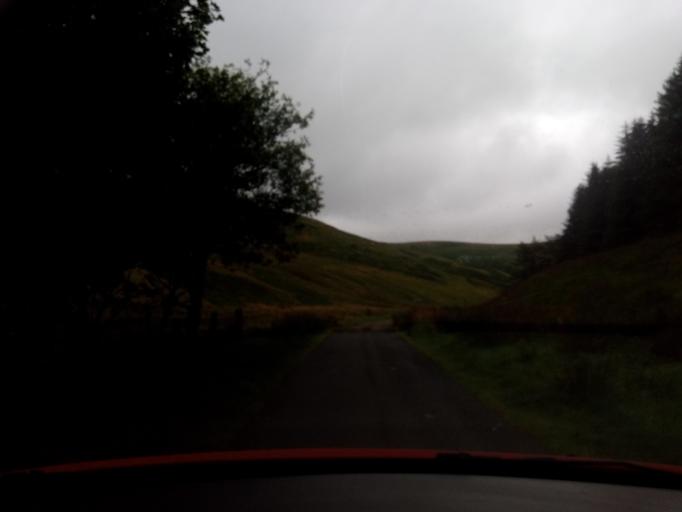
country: GB
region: England
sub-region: Northumberland
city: Rochester
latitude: 55.3981
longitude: -2.2548
